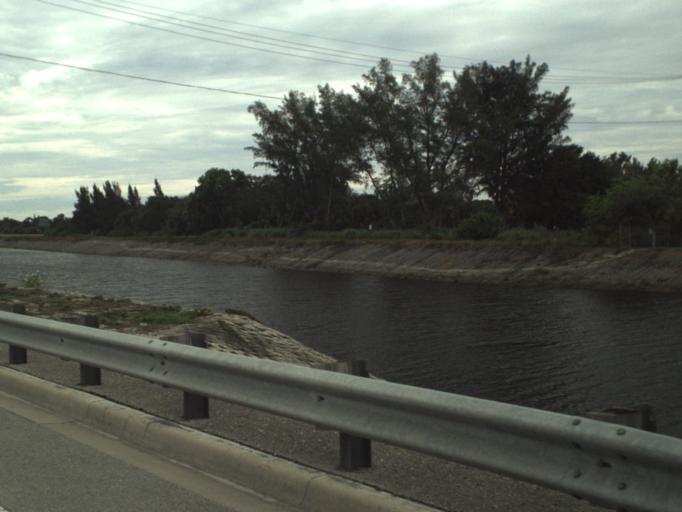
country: US
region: Florida
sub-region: Palm Beach County
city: Haverhill
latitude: 26.6771
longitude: -80.0921
